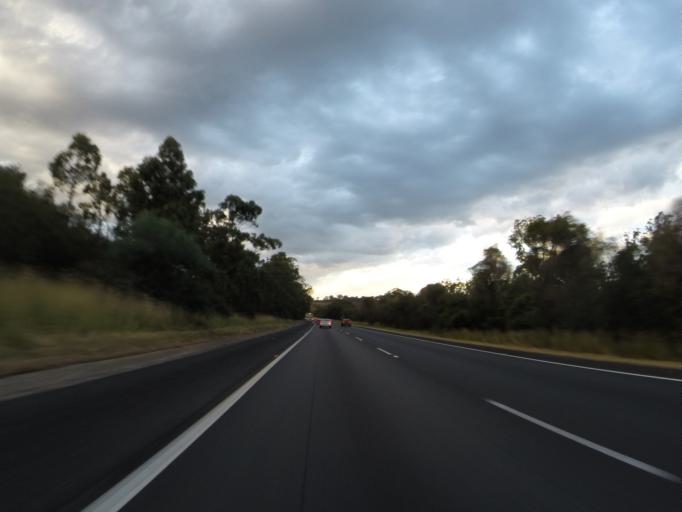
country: AU
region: New South Wales
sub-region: Campbelltown Municipality
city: Glen Alpine
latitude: -34.1222
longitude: 150.7544
